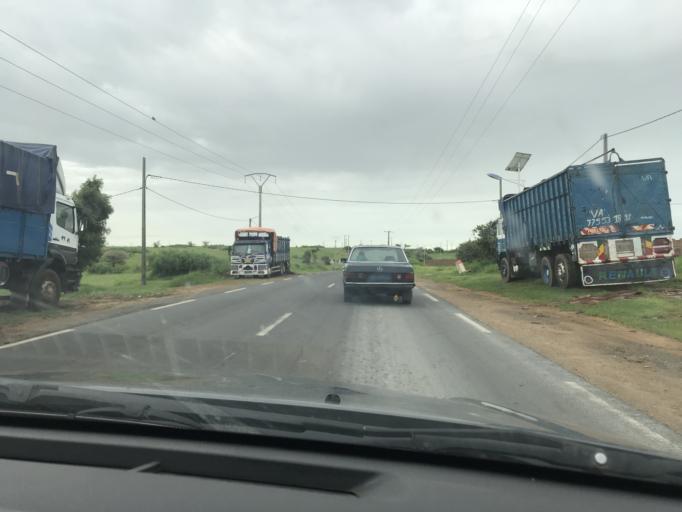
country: SN
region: Thies
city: Mekhe
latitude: 15.1207
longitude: -16.9095
